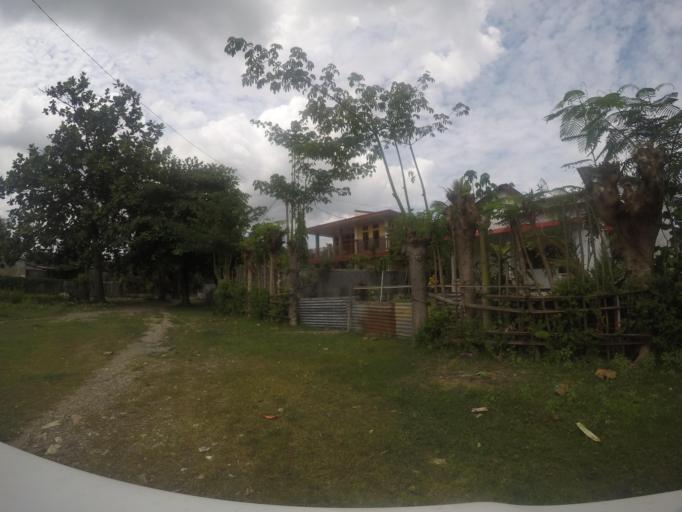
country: TL
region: Viqueque
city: Viqueque
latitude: -8.8588
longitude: 126.3643
